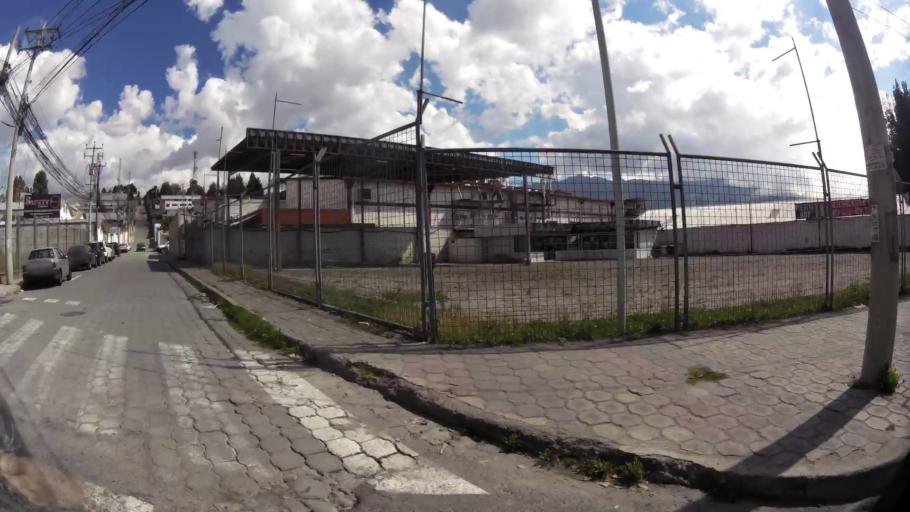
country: EC
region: Pichincha
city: Quito
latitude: -0.1170
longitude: -78.4732
